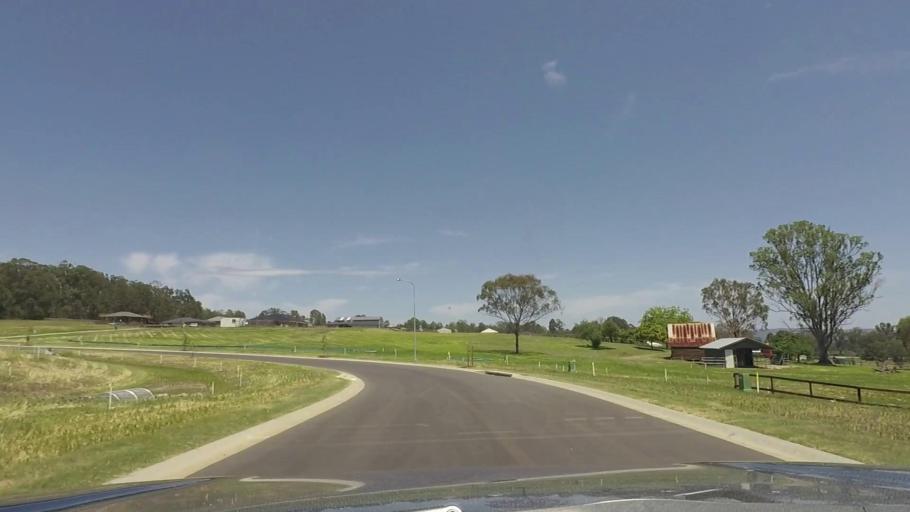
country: AU
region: Queensland
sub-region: Logan
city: Cedar Vale
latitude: -27.8892
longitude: 152.9871
